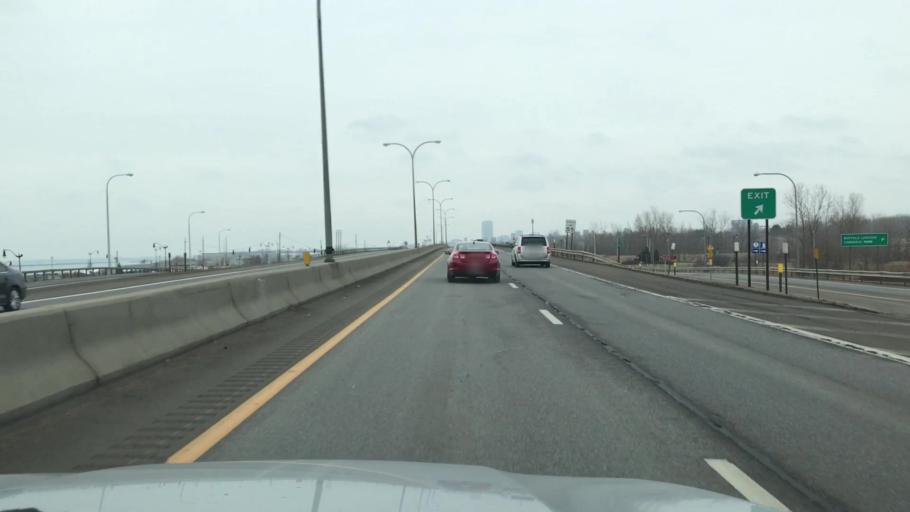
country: US
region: New York
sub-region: Erie County
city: Lackawanna
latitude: 42.8373
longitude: -78.8556
